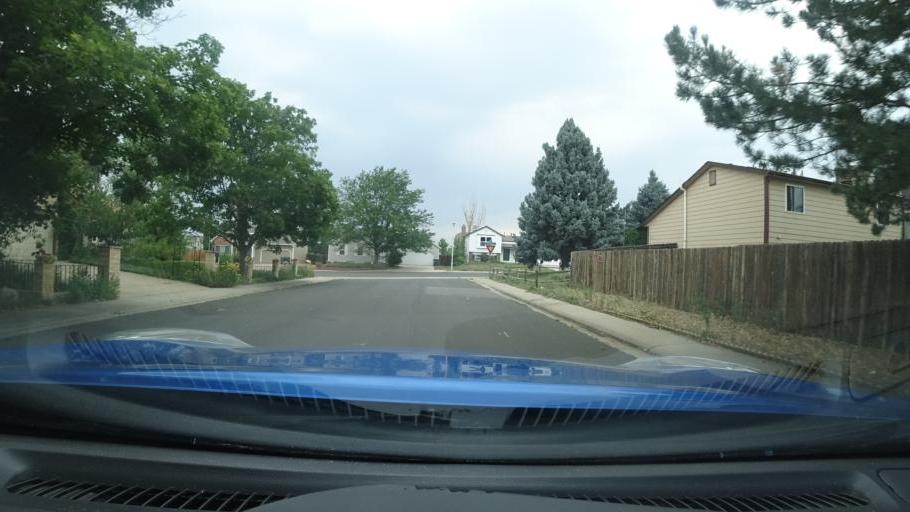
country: US
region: Colorado
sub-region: Adams County
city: Aurora
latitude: 39.6886
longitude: -104.7623
